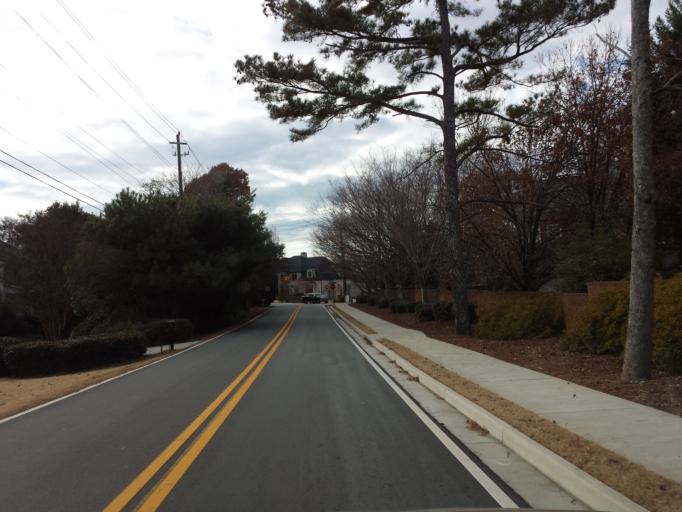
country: US
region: Georgia
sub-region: Fulton County
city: Sandy Springs
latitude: 33.9563
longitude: -84.4190
